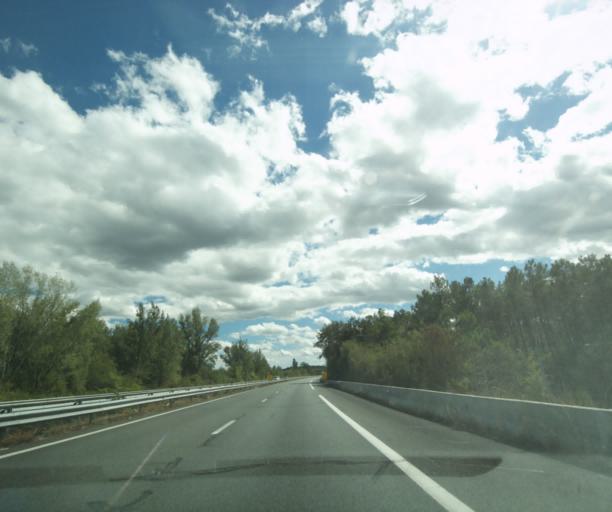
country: FR
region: Aquitaine
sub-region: Departement de la Gironde
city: Gironde-sur-Dropt
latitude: 44.5295
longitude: -0.0920
